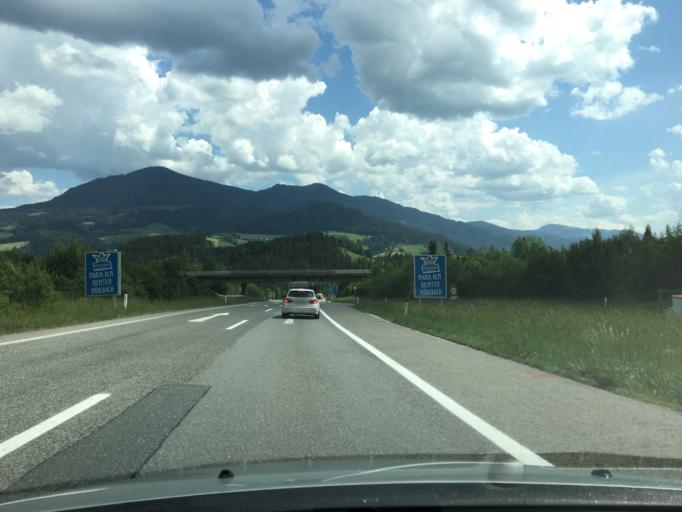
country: AT
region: Salzburg
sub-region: Politischer Bezirk Sankt Johann im Pongau
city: Bischofshofen
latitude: 47.4397
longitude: 13.2222
